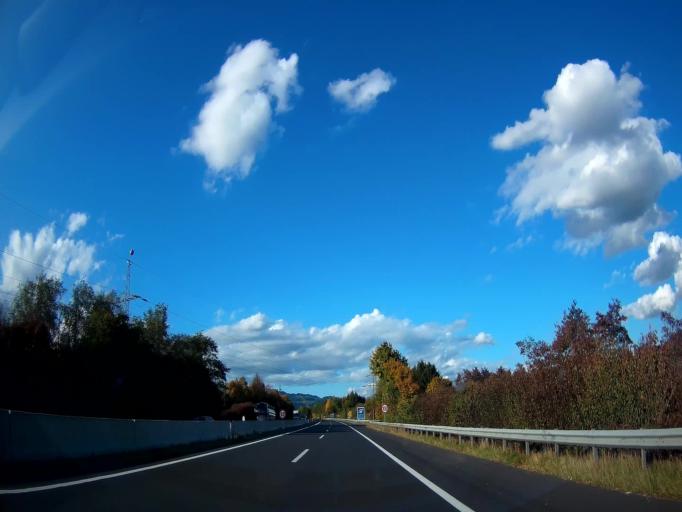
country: AT
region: Carinthia
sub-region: Politischer Bezirk Wolfsberg
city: Wolfsberg
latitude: 46.8154
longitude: 14.8228
